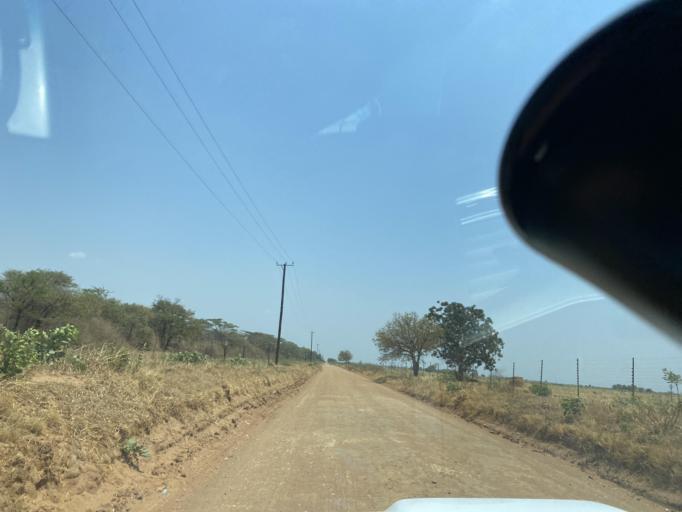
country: ZM
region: Lusaka
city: Lusaka
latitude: -15.4379
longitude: 28.0662
